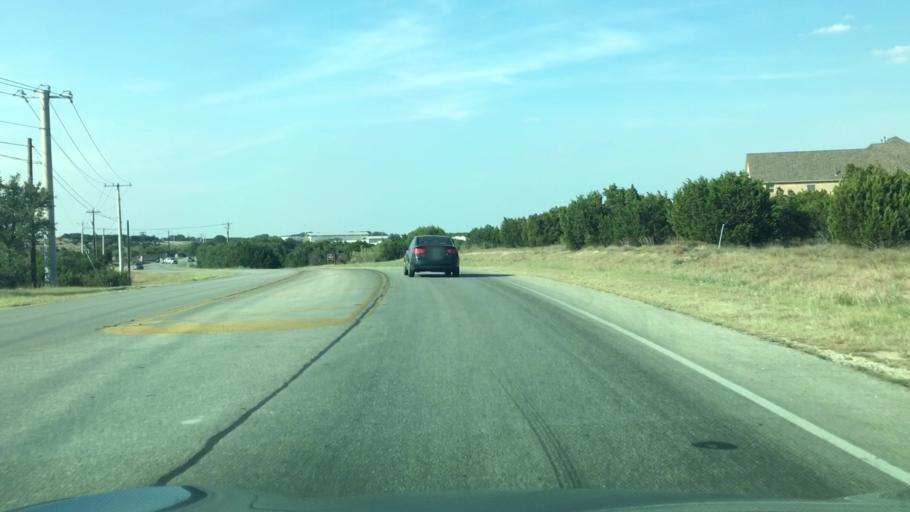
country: US
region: Texas
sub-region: Hays County
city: Dripping Springs
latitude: 30.1718
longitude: -98.0052
